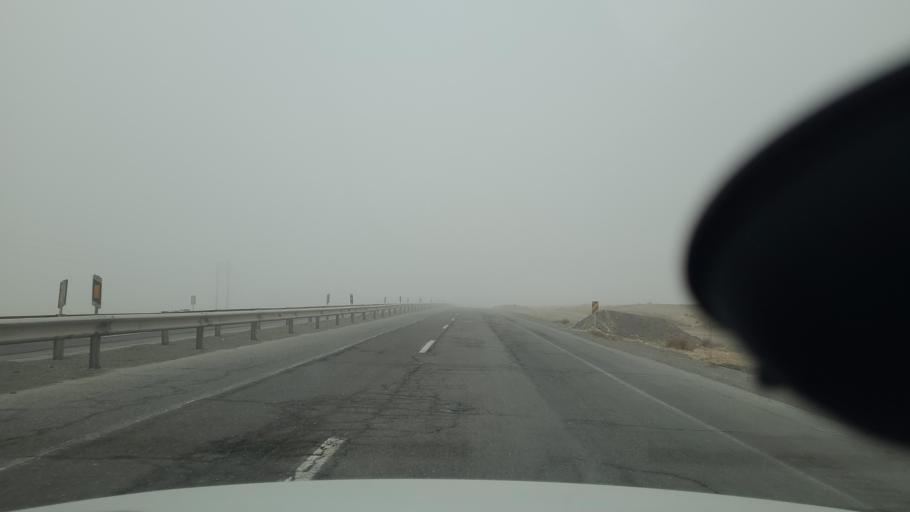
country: IR
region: Razavi Khorasan
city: Fariman
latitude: 35.7609
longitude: 59.7480
